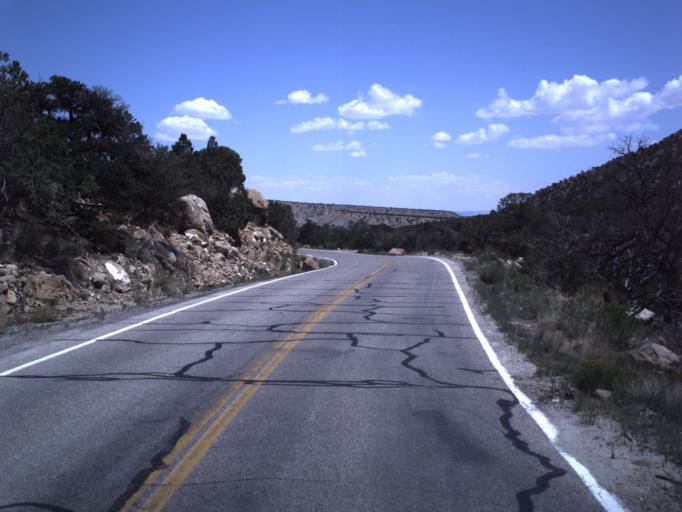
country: US
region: Utah
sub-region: Emery County
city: Orangeville
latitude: 39.2756
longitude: -111.1863
